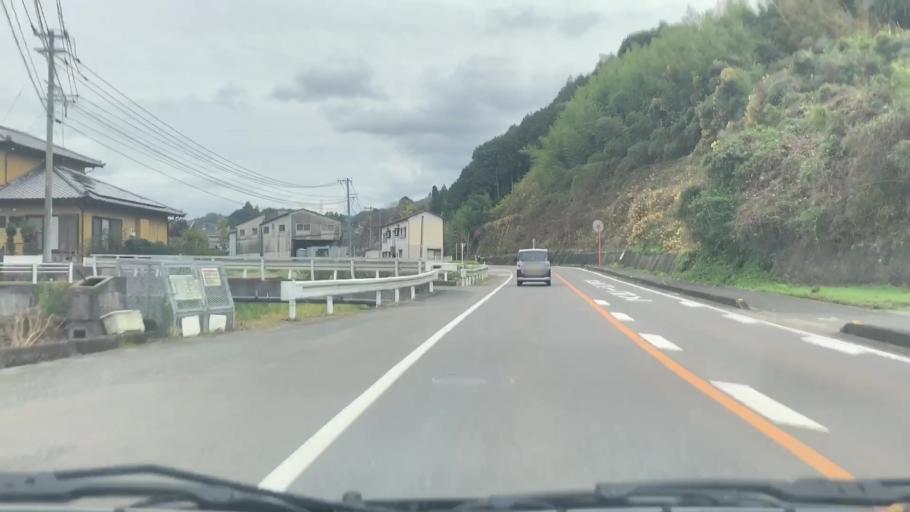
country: JP
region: Saga Prefecture
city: Ureshinomachi-shimojuku
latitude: 33.0999
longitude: 130.0007
